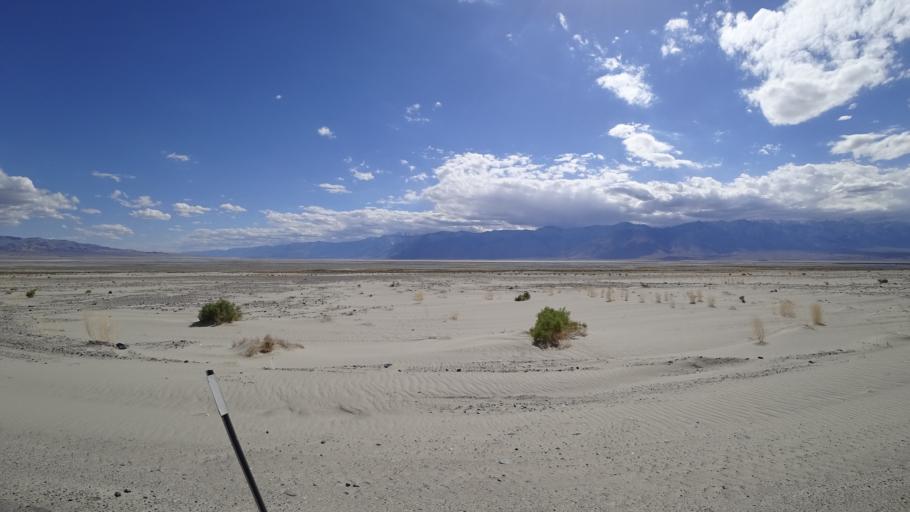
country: US
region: California
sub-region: Inyo County
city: Lone Pine
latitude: 36.5041
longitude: -117.8866
